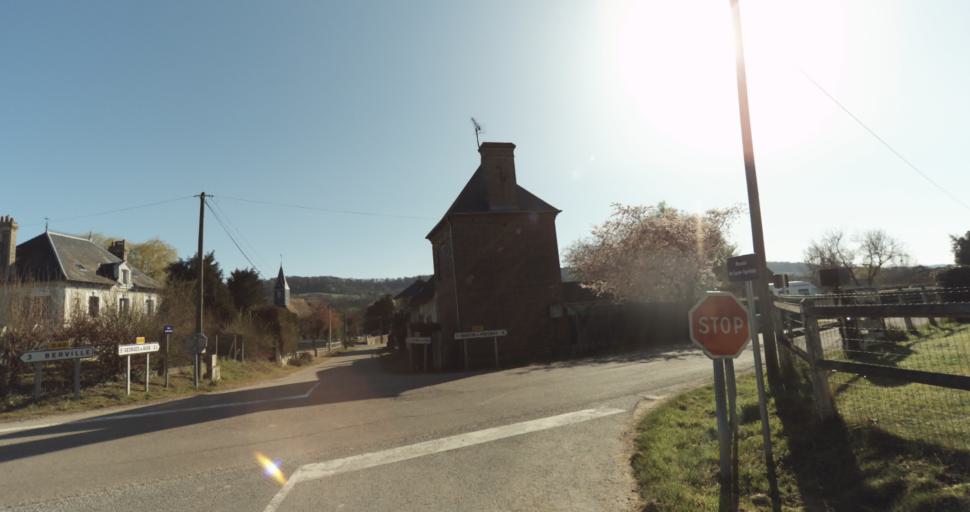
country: FR
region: Lower Normandy
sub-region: Departement du Calvados
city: Saint-Pierre-sur-Dives
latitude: 48.9885
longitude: 0.0282
